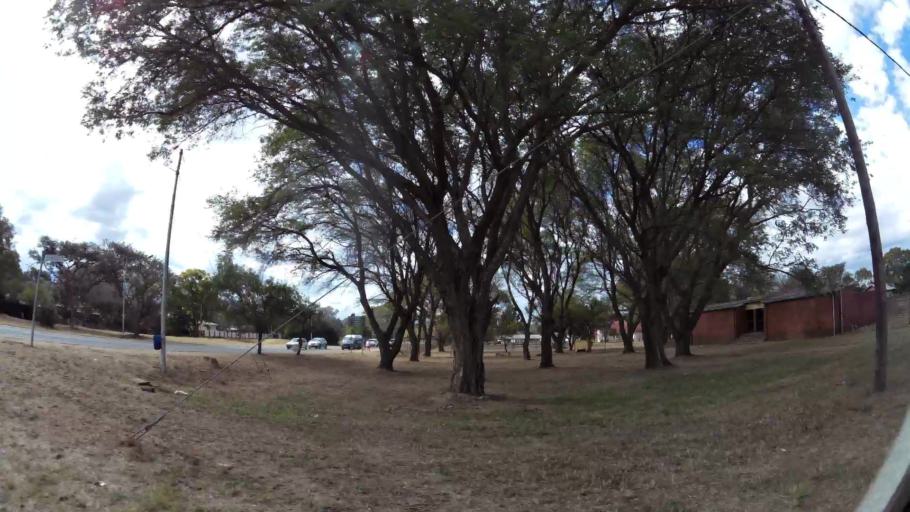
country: ZA
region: Limpopo
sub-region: Waterberg District Municipality
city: Modimolle
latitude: -24.7050
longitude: 28.4000
